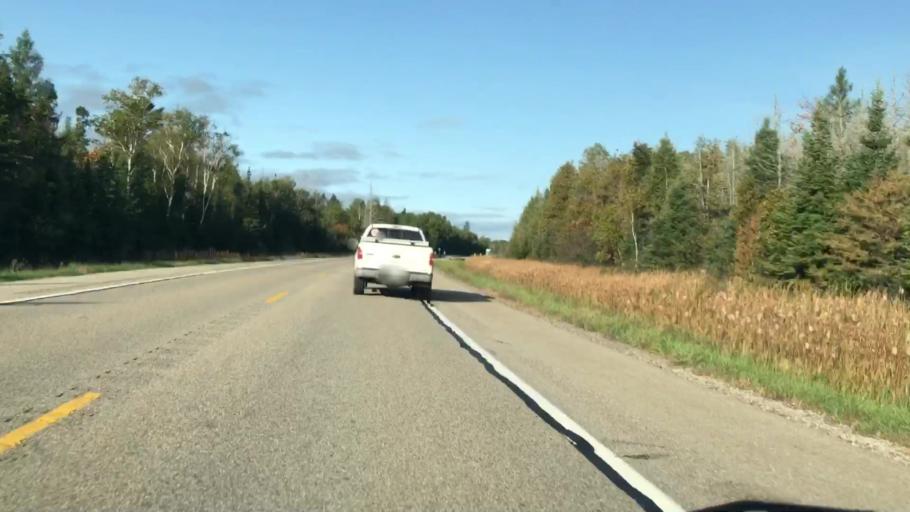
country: US
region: Michigan
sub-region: Luce County
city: Newberry
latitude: 46.3038
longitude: -85.2265
